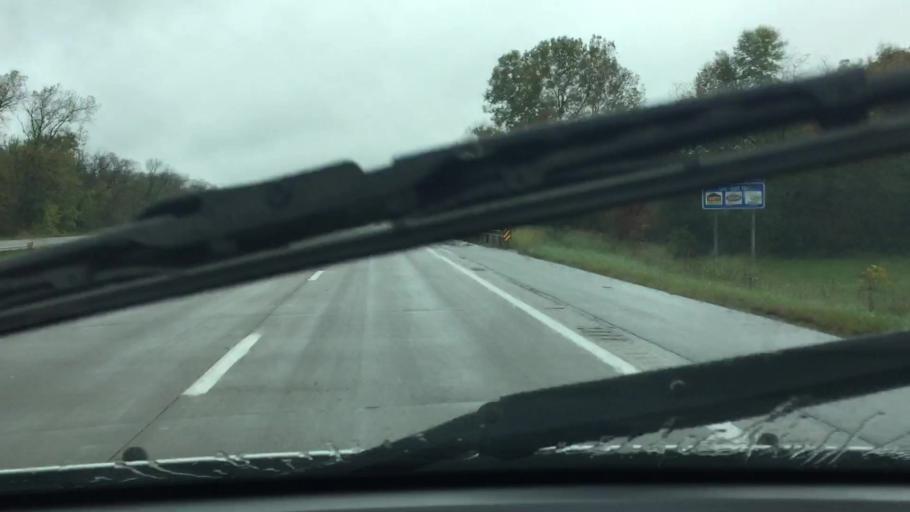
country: US
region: Iowa
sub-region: Jasper County
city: Colfax
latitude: 41.6989
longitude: -93.2151
